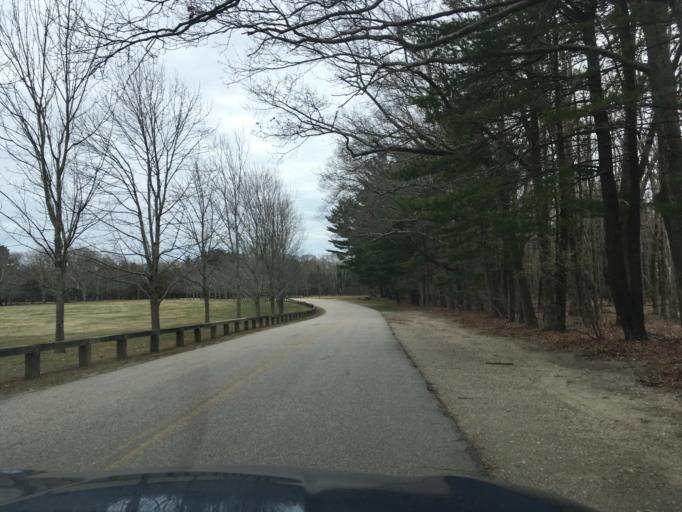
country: US
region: Rhode Island
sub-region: Kent County
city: East Greenwich
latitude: 41.6566
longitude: -71.4410
